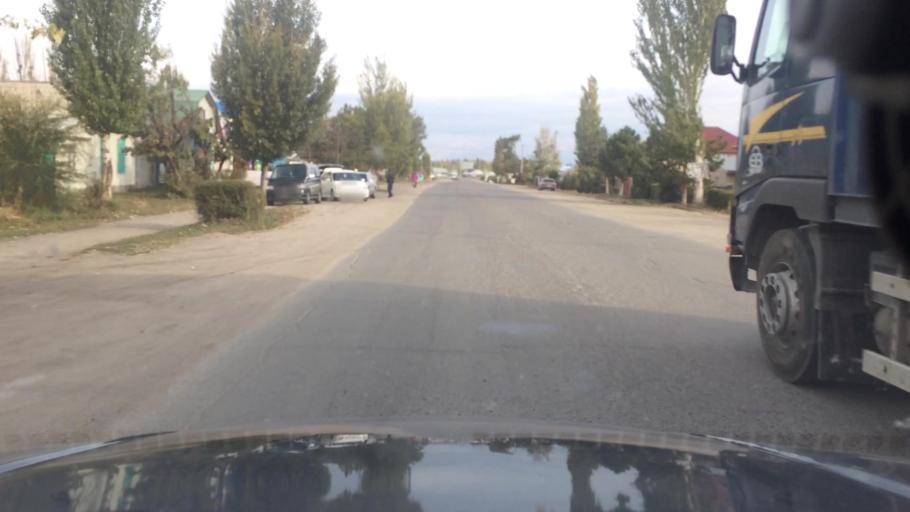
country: KG
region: Ysyk-Koel
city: Karakol
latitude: 42.5195
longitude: 78.3858
